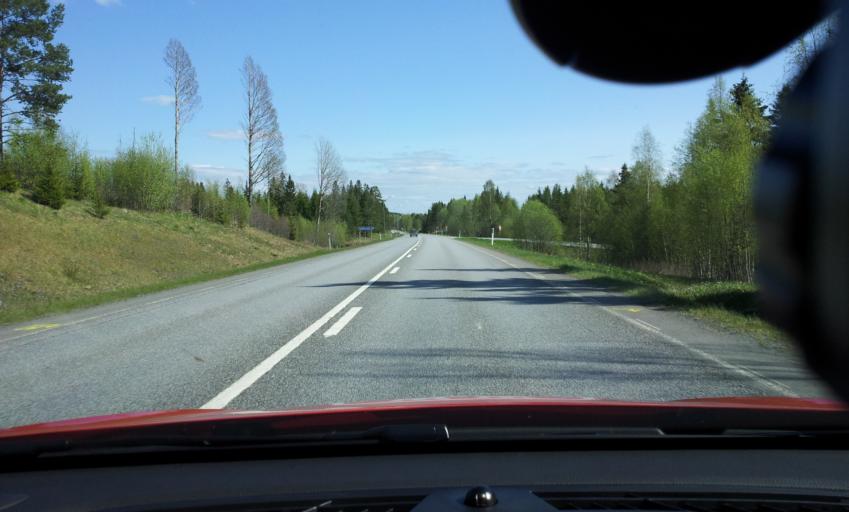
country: SE
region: Jaemtland
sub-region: Krokoms Kommun
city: Valla
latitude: 63.3258
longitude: 14.0468
